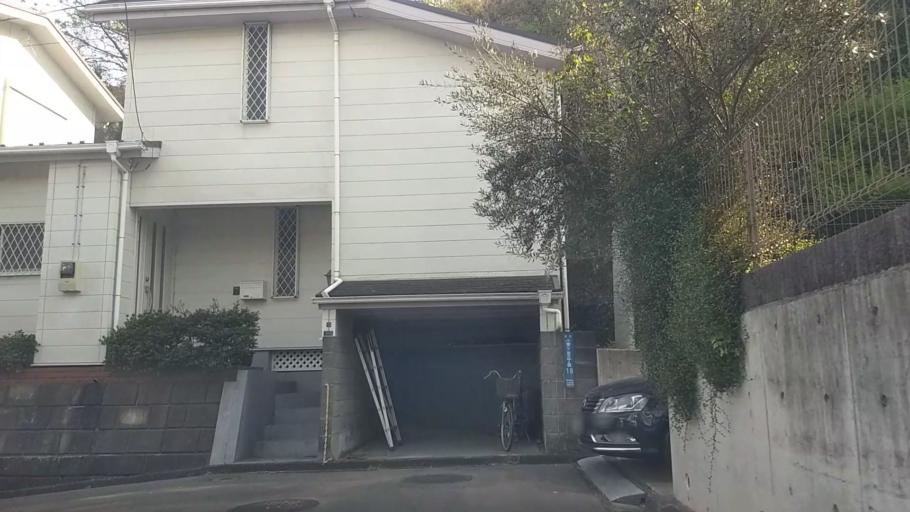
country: JP
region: Kanagawa
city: Kamakura
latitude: 35.3701
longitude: 139.5523
